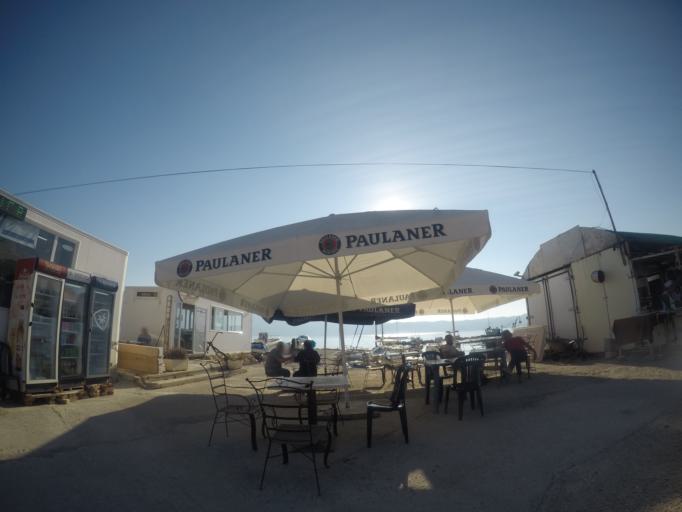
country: AL
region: Vlore
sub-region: Rrethi i Vlores
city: Orikum
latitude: 40.3615
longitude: 19.4803
